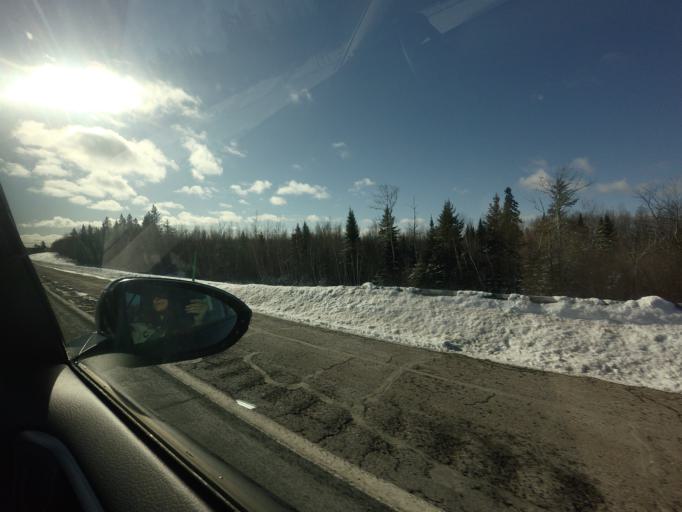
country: CA
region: New Brunswick
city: Fredericton
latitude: 45.8958
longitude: -66.6488
